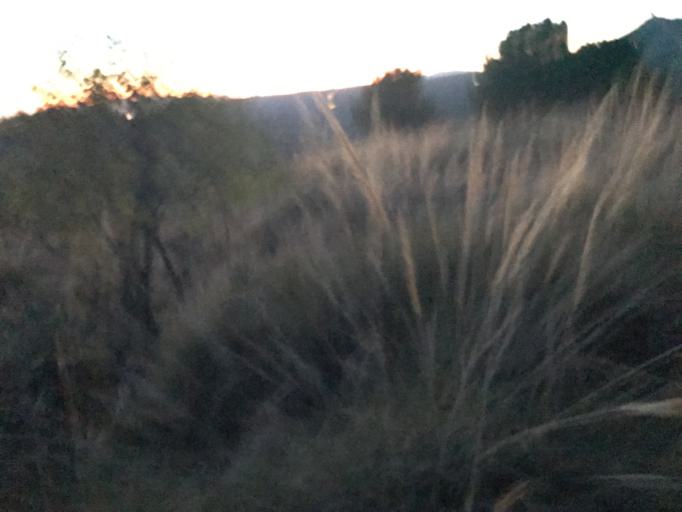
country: ES
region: Andalusia
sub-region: Provincia de Granada
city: Beas de Granada
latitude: 37.2139
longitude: -3.4740
